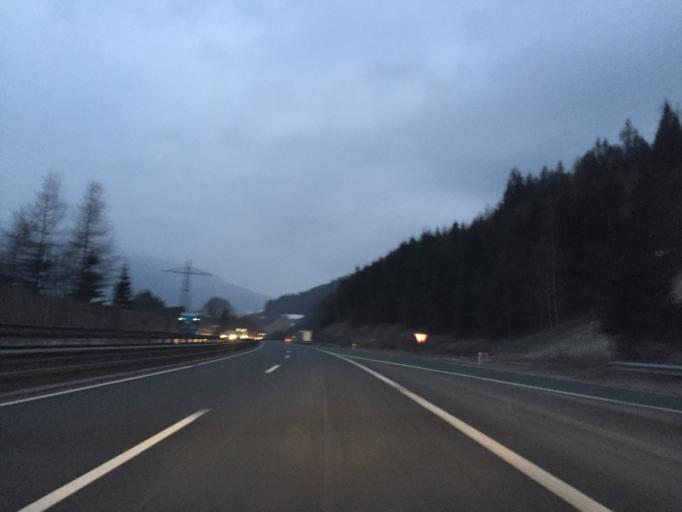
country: AT
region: Salzburg
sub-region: Politischer Bezirk Sankt Johann im Pongau
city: Huttau
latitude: 47.4265
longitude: 13.3438
